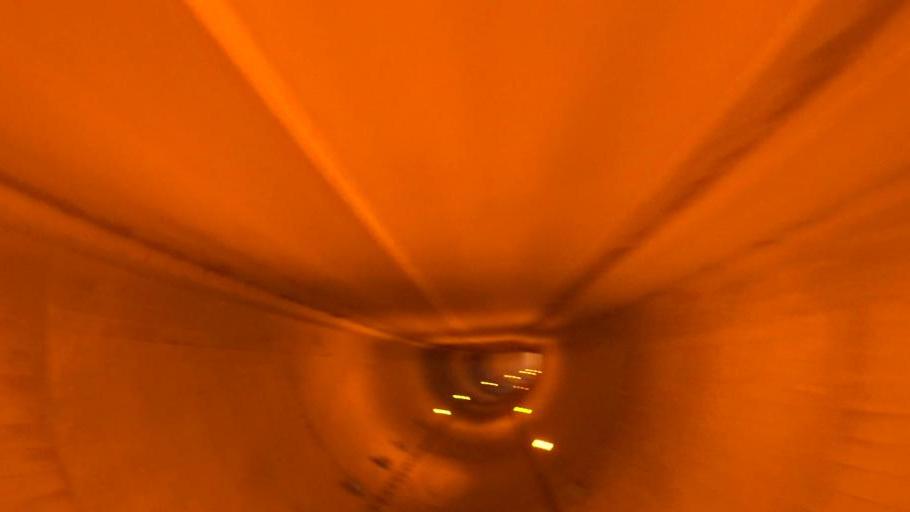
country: JP
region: Kyoto
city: Maizuru
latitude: 35.4734
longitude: 135.3157
